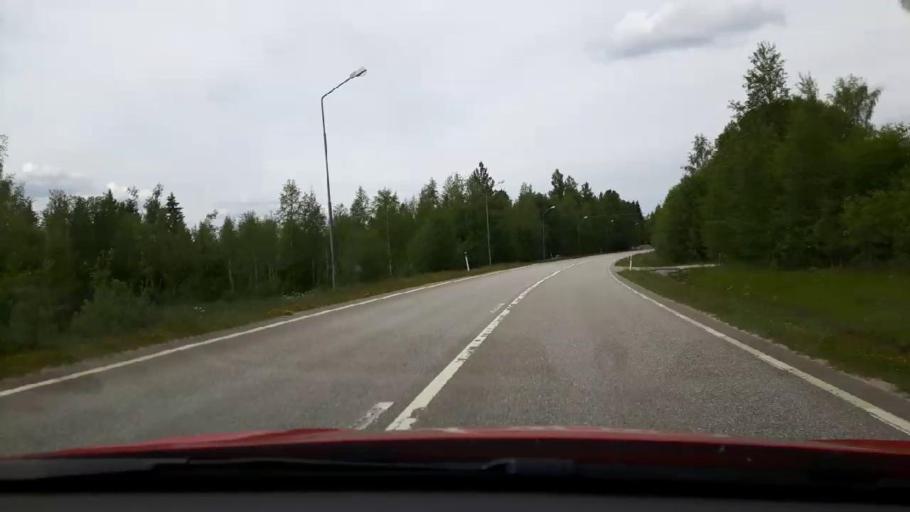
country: SE
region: Jaemtland
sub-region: Harjedalens Kommun
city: Sveg
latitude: 62.0629
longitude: 14.2788
